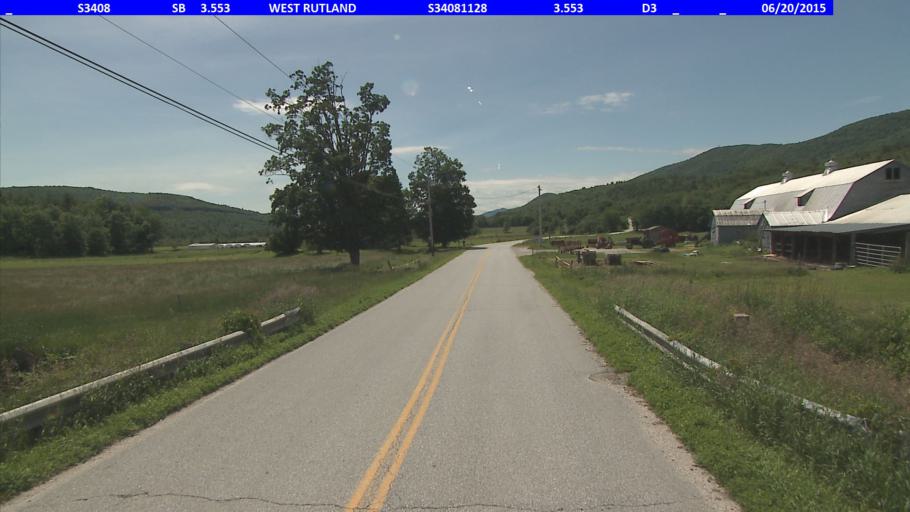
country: US
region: Vermont
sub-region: Rutland County
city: West Rutland
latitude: 43.6599
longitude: -73.0736
